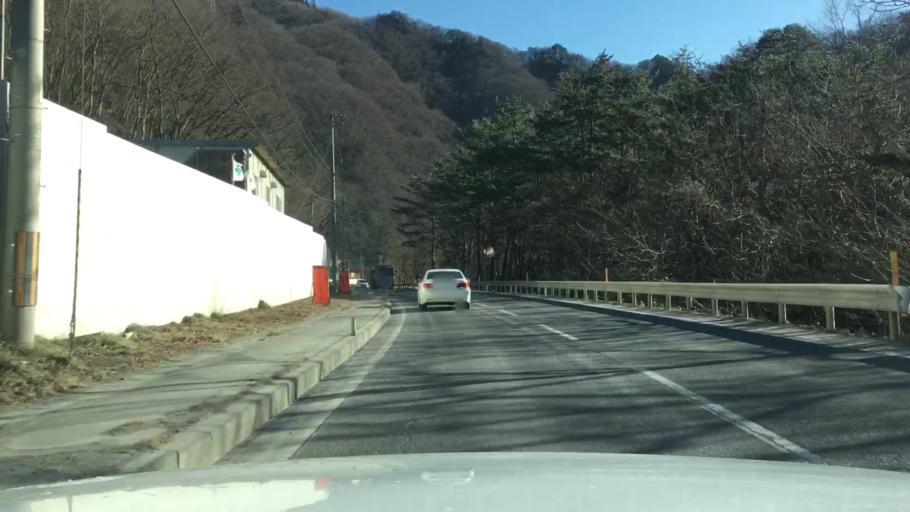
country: JP
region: Iwate
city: Miyako
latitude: 39.6010
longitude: 141.7056
